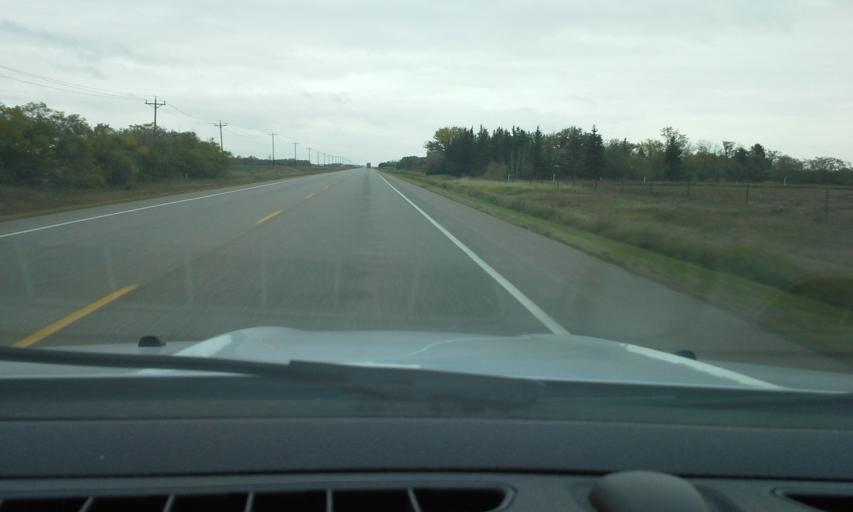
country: CA
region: Saskatchewan
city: Lloydminster
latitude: 53.2780
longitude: -109.8480
